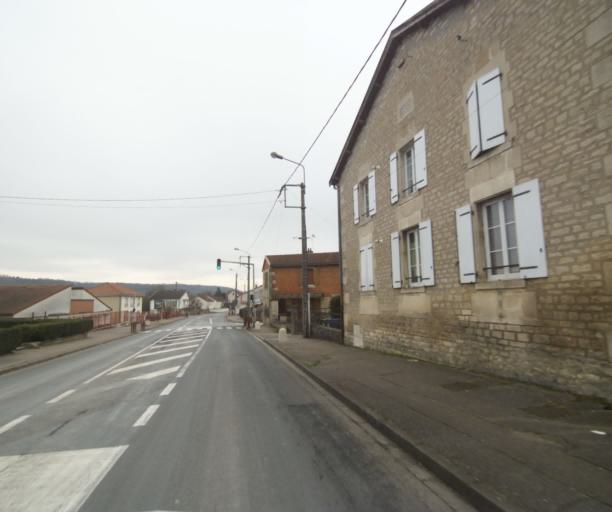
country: FR
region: Champagne-Ardenne
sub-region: Departement de la Haute-Marne
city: Chevillon
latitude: 48.5262
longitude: 5.1011
